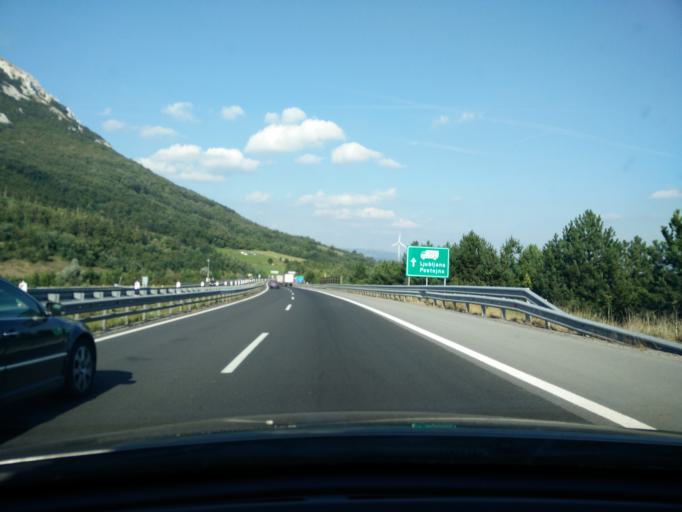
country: SI
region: Divaca
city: Divaca
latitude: 45.7552
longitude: 14.0509
